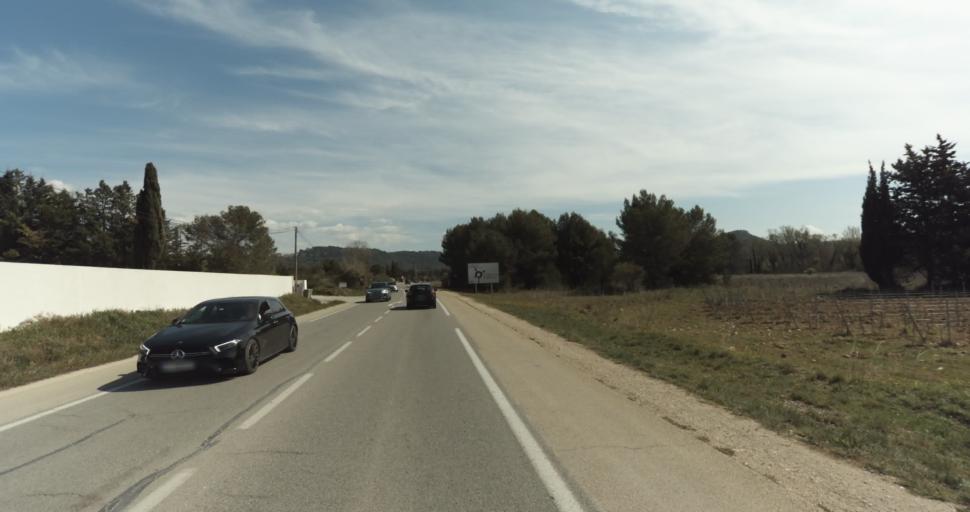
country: FR
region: Provence-Alpes-Cote d'Azur
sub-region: Departement des Bouches-du-Rhone
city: Velaux
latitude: 43.5408
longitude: 5.2642
